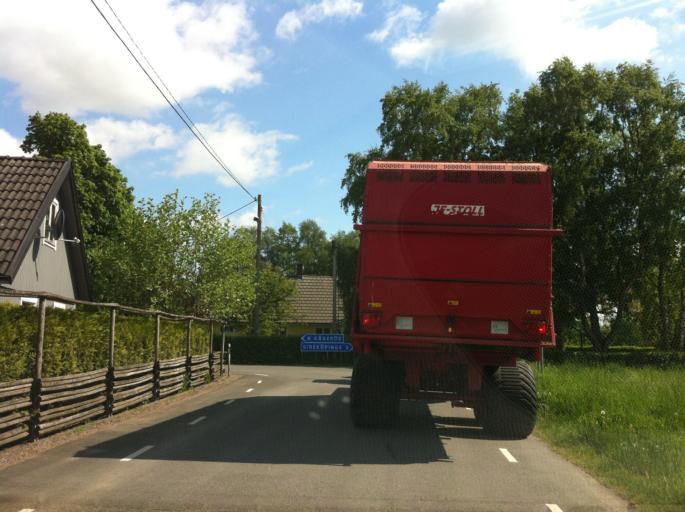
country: SE
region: Skane
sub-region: Landskrona
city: Asmundtorp
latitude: 55.9453
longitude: 12.9170
